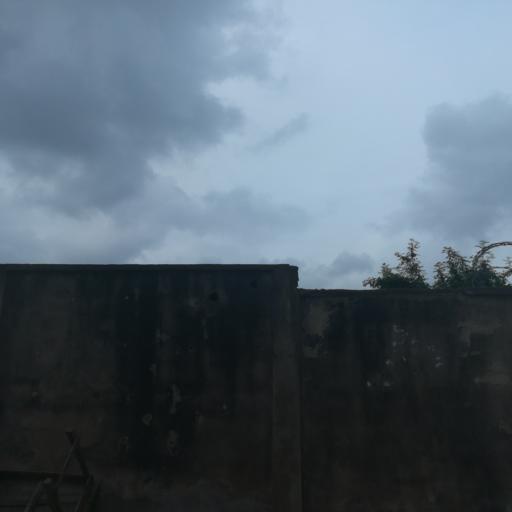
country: NG
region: Lagos
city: Ojota
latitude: 6.5886
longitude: 3.3864
